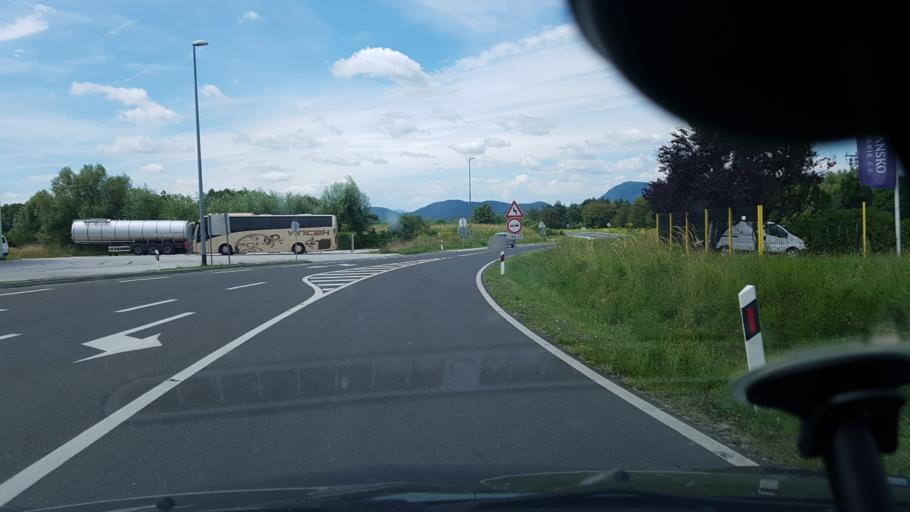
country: HR
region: Varazdinska
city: Ivanec
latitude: 46.2261
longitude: 16.1096
